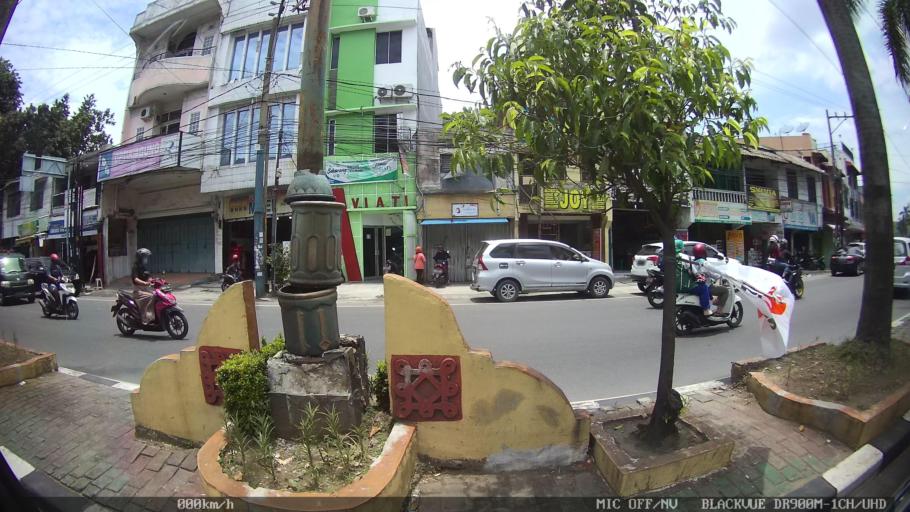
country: ID
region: North Sumatra
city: Medan
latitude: 3.5709
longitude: 98.6603
